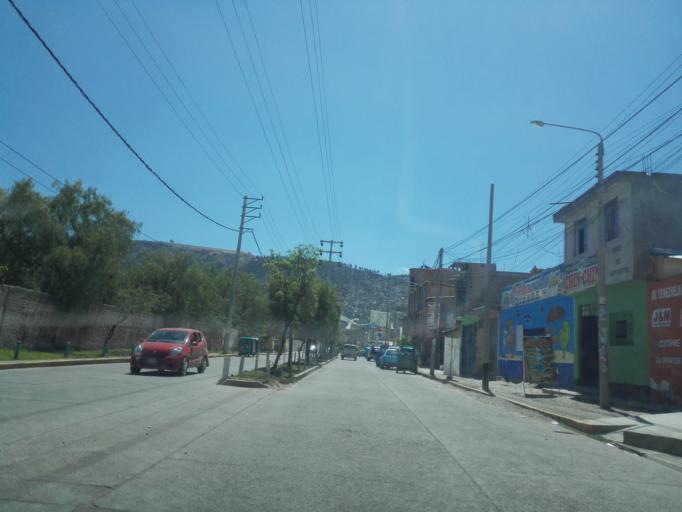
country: PE
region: Ayacucho
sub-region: Provincia de Huamanga
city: Ayacucho
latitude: -13.1547
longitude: -74.2197
